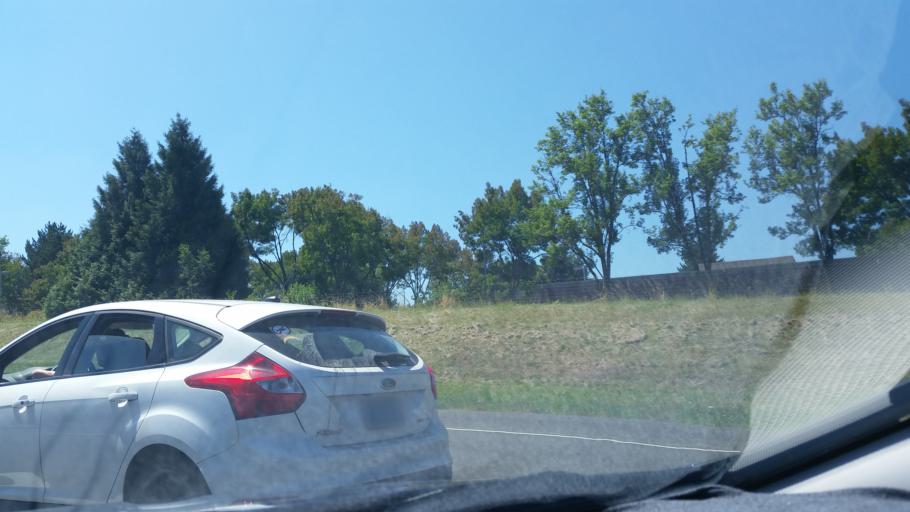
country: US
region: Oregon
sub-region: Washington County
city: Tualatin
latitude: 45.3770
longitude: -122.7550
